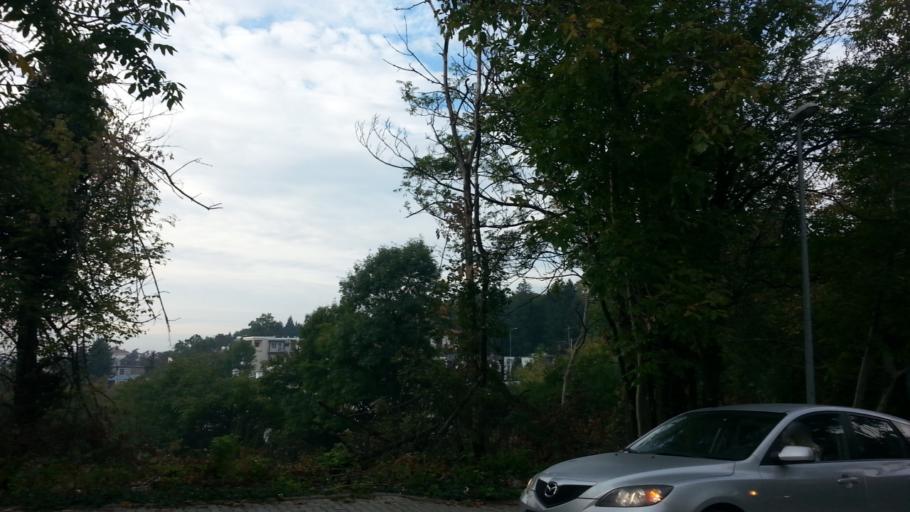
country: RS
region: Central Serbia
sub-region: Belgrade
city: Savski Venac
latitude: 44.7697
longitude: 20.4550
